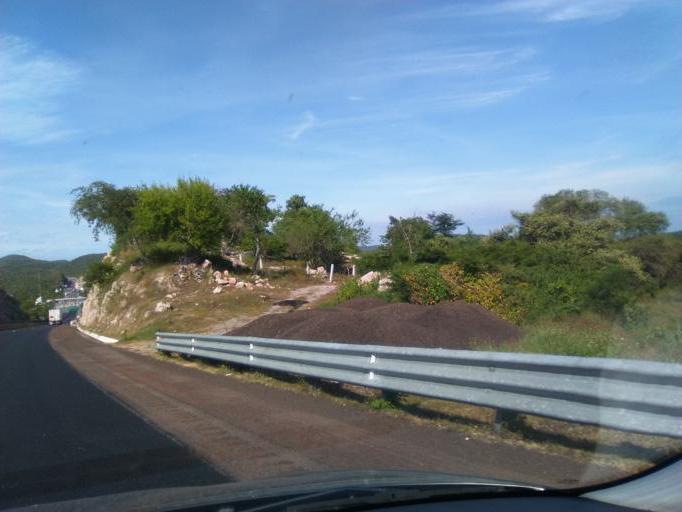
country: MX
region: Guerrero
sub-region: Huitzuco de los Figueroa
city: Ciudad de Huitzuco
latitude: 18.2229
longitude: -99.2173
